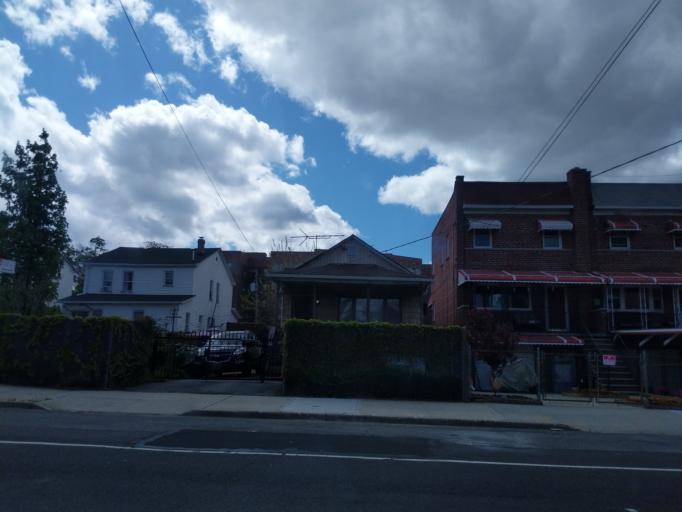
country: US
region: New York
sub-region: Bronx
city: The Bronx
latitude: 40.8687
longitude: -73.8615
